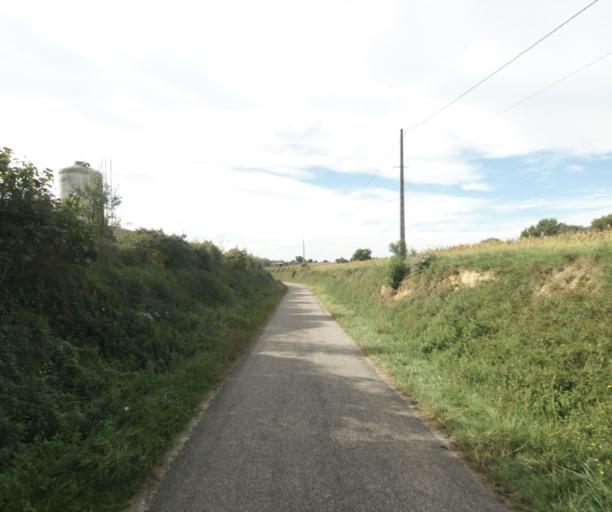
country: FR
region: Midi-Pyrenees
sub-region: Departement du Gers
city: Le Houga
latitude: 43.8678
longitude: -0.1490
